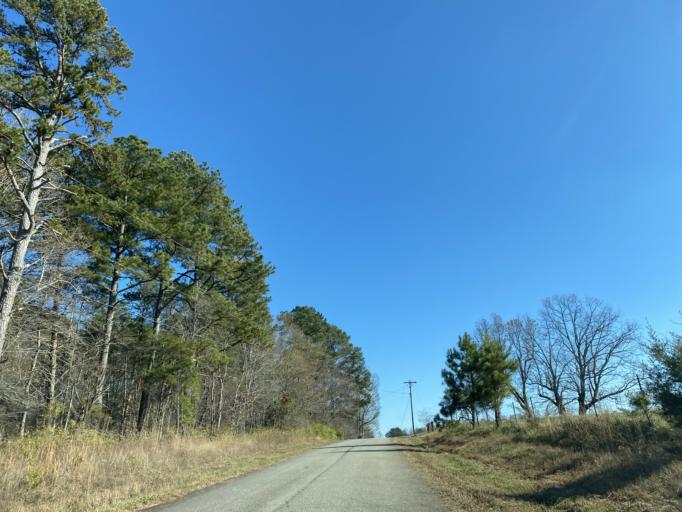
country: US
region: South Carolina
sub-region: Spartanburg County
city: Mayo
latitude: 35.1459
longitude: -81.7780
